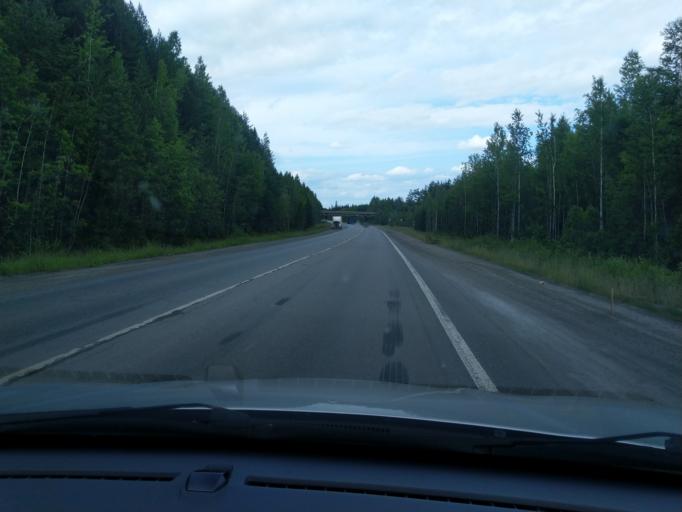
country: RU
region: Sverdlovsk
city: Nizhniy Tagil
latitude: 57.9226
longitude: 59.8516
